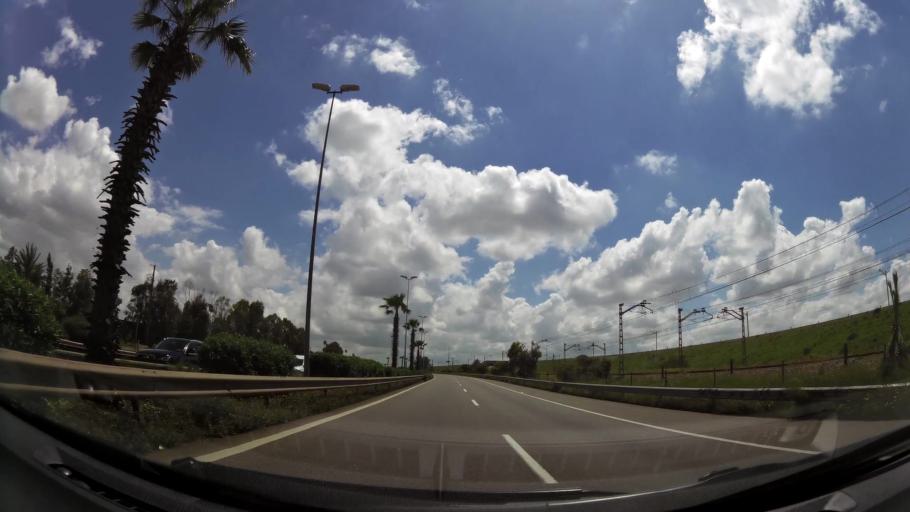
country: MA
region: Chaouia-Ouardigha
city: Nouaseur
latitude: 33.4119
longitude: -7.6264
